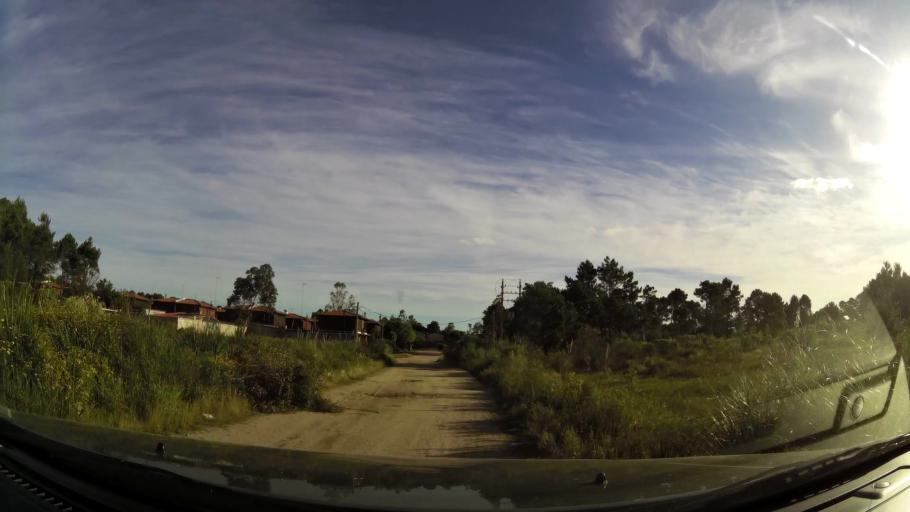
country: UY
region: Canelones
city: Empalme Olmos
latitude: -34.7655
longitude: -55.8581
